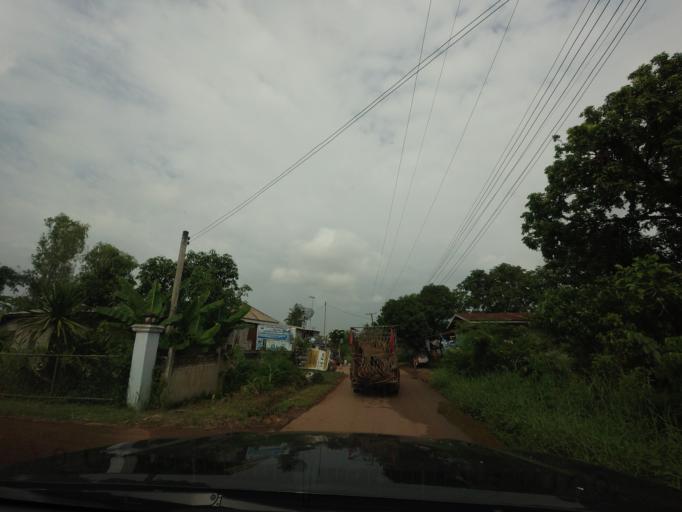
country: TH
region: Nong Khai
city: Nong Khai
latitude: 17.8172
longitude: 102.7145
